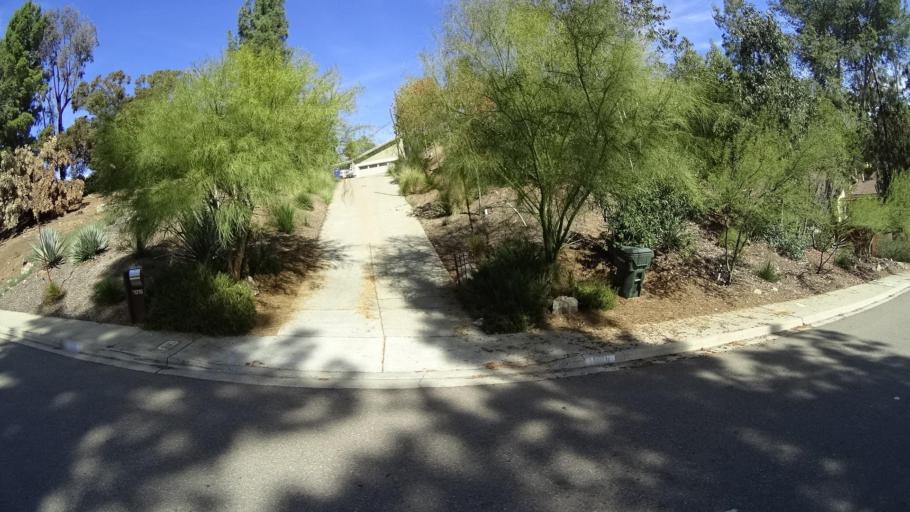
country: US
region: California
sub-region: San Diego County
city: Casa de Oro-Mount Helix
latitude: 32.7542
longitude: -116.9560
